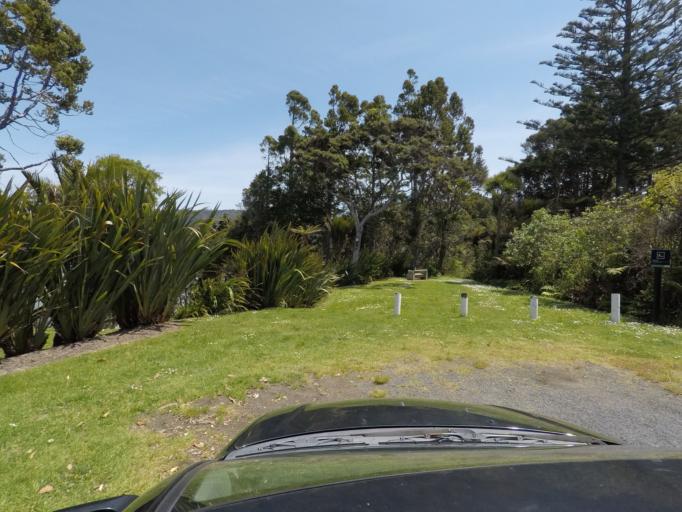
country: NZ
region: Auckland
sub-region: Auckland
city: Titirangi
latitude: -36.9776
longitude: 174.6311
